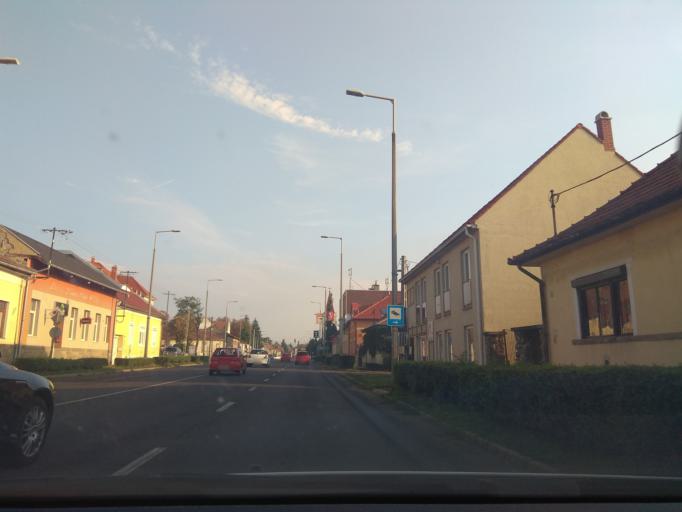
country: HU
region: Heves
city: Eger
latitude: 47.8974
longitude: 20.3678
